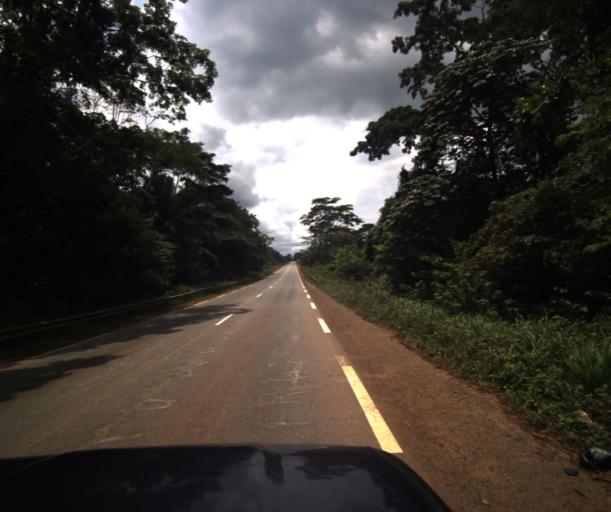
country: CM
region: Centre
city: Eseka
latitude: 3.8780
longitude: 10.6824
